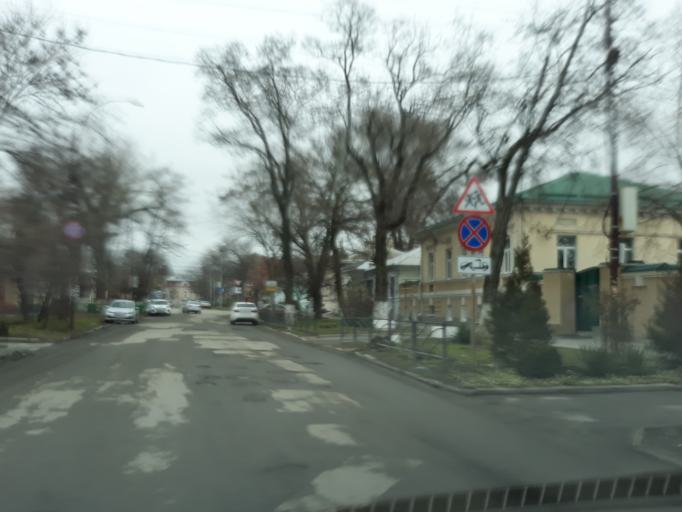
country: RU
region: Rostov
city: Taganrog
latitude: 47.2087
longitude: 38.9309
